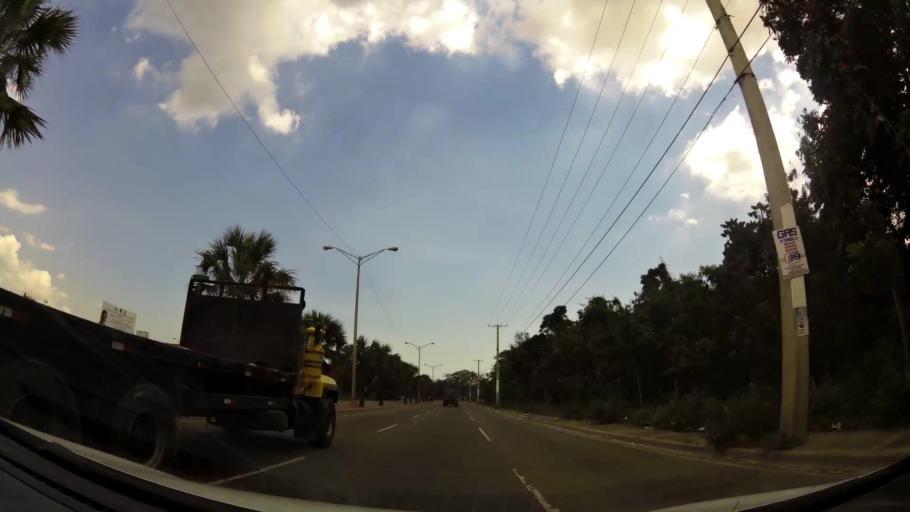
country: DO
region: Nacional
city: La Agustina
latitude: 18.5322
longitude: -69.9553
